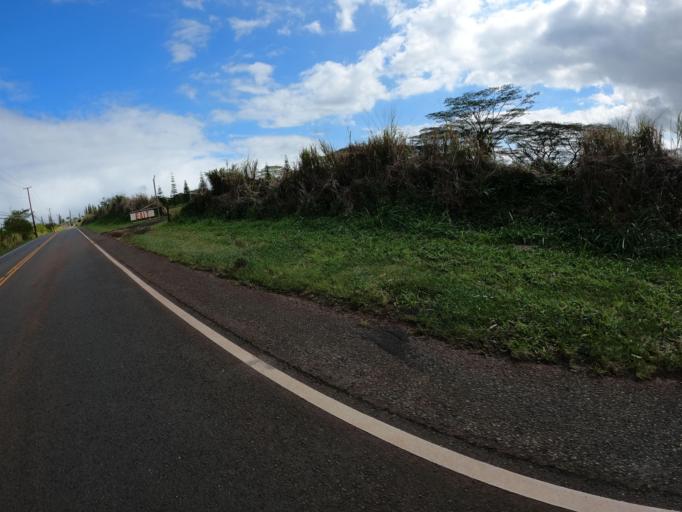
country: US
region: Hawaii
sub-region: Honolulu County
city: Whitmore Village
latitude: 21.5137
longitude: -158.0108
